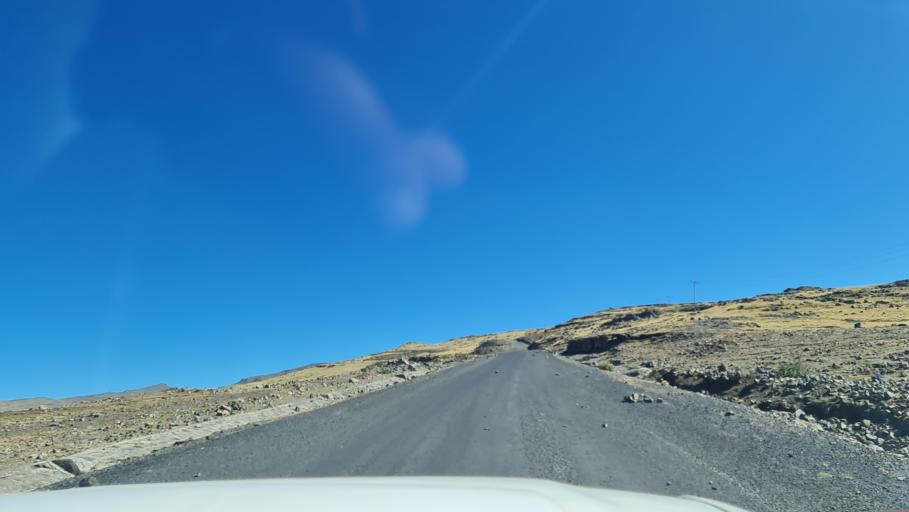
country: ET
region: Amhara
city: Debark'
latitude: 13.1558
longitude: 38.1864
